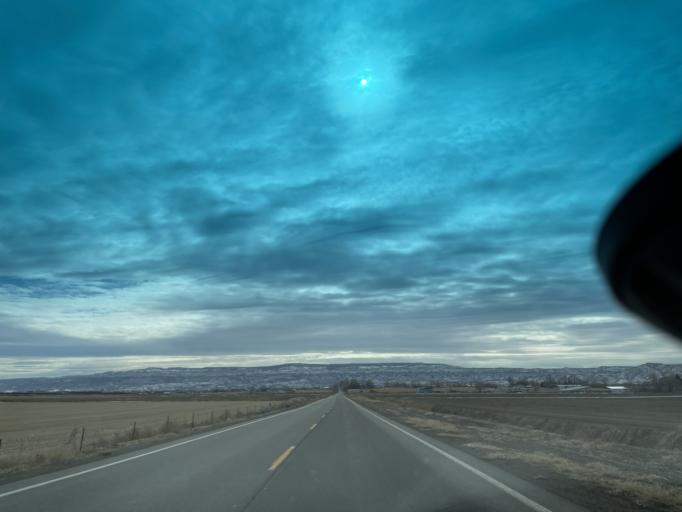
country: US
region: Colorado
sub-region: Mesa County
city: Loma
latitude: 39.2351
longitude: -108.8130
